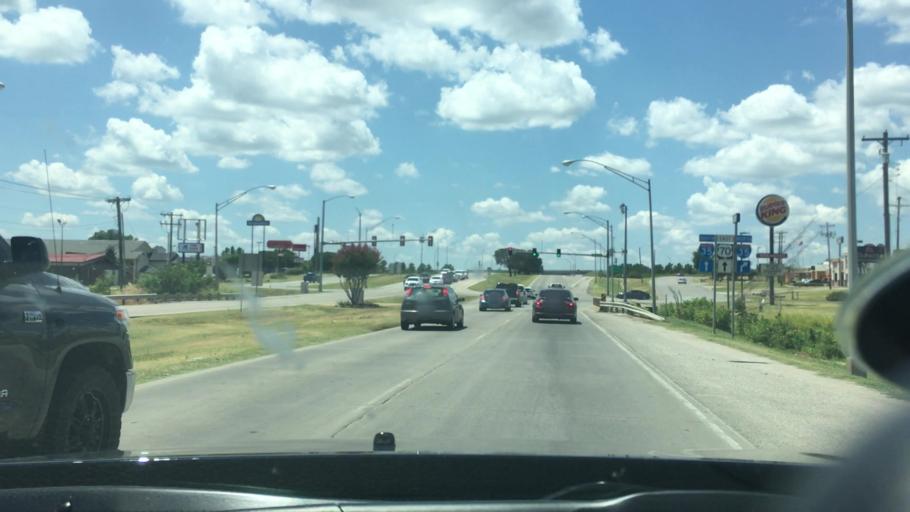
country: US
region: Oklahoma
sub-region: Carter County
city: Ardmore
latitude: 34.1730
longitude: -97.1613
